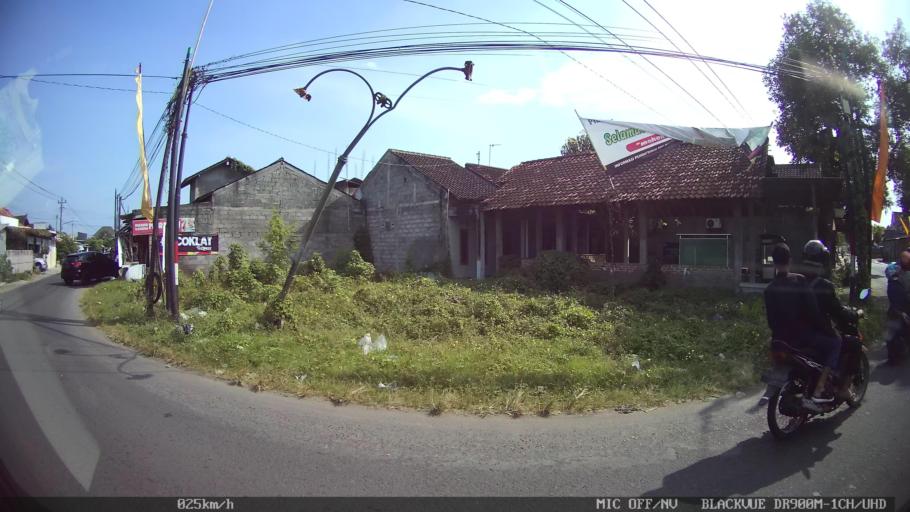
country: ID
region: Daerah Istimewa Yogyakarta
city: Kasihan
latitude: -7.8433
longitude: 110.3348
